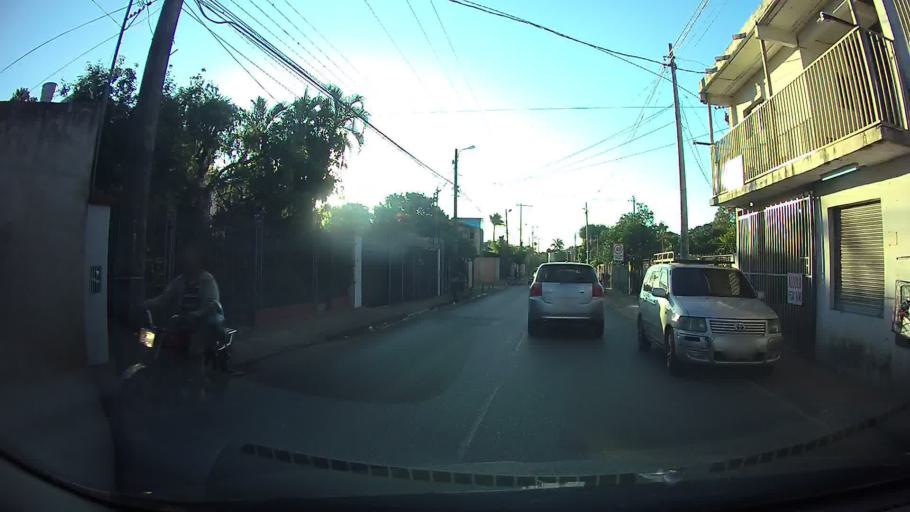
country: PY
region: Central
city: Fernando de la Mora
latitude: -25.3324
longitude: -57.5467
